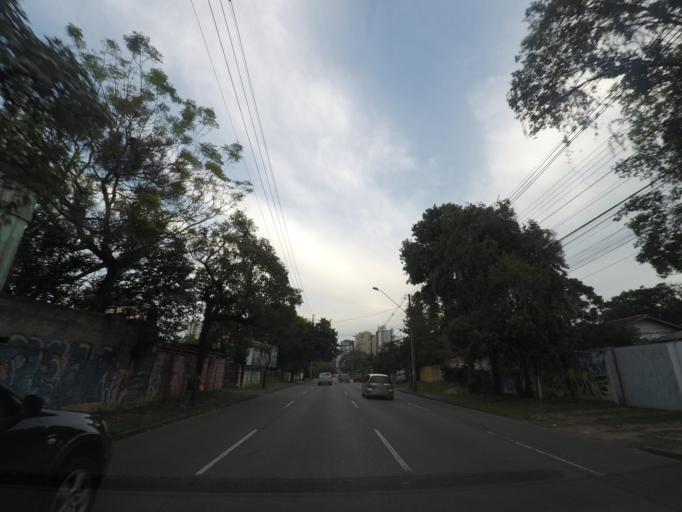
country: BR
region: Parana
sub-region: Curitiba
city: Curitiba
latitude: -25.4026
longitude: -49.2503
